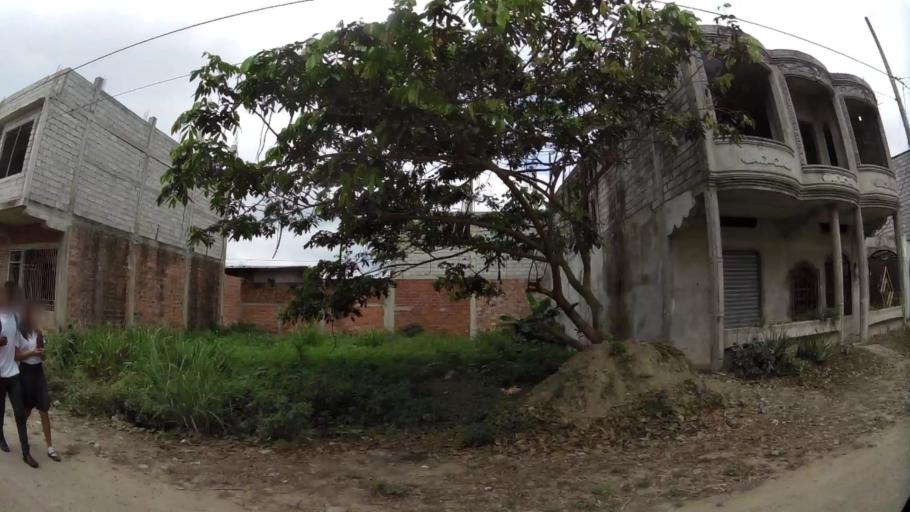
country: EC
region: Guayas
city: Naranjal
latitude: -2.6813
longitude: -79.6193
